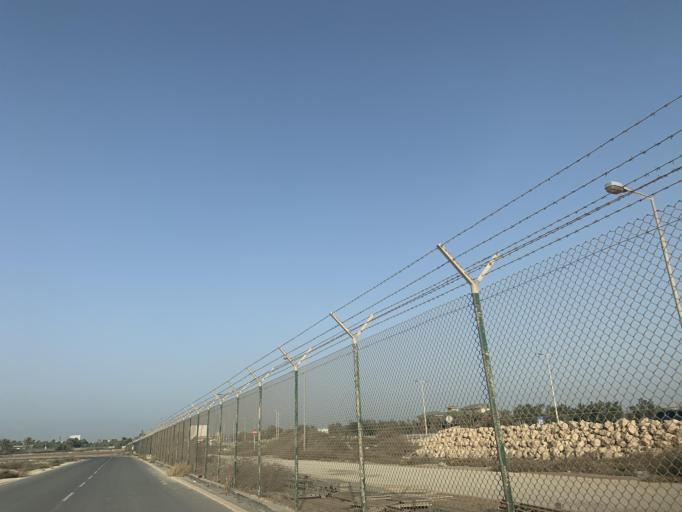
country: BH
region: Central Governorate
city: Madinat Hamad
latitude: 26.1723
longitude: 50.4499
